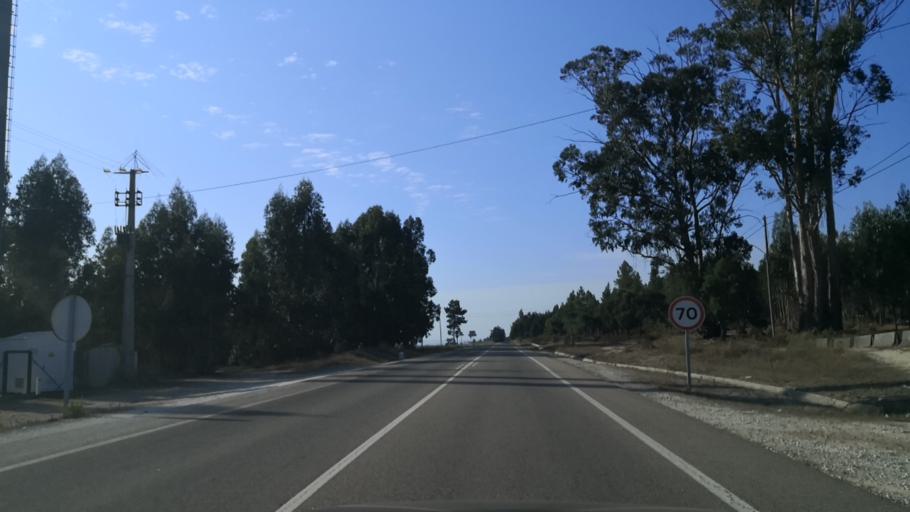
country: PT
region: Santarem
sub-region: Almeirim
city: Fazendas de Almeirim
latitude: 39.1177
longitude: -8.5971
